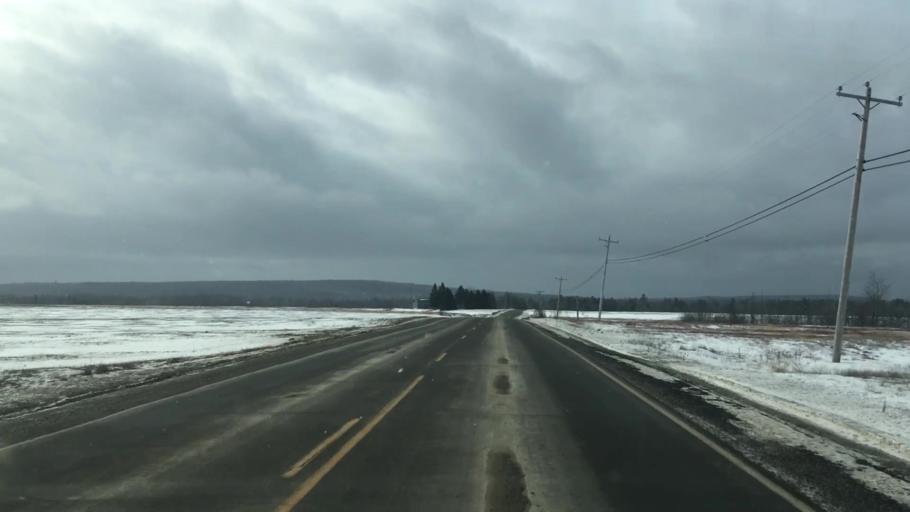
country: US
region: Maine
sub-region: Washington County
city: Calais
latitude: 45.0260
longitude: -67.3741
